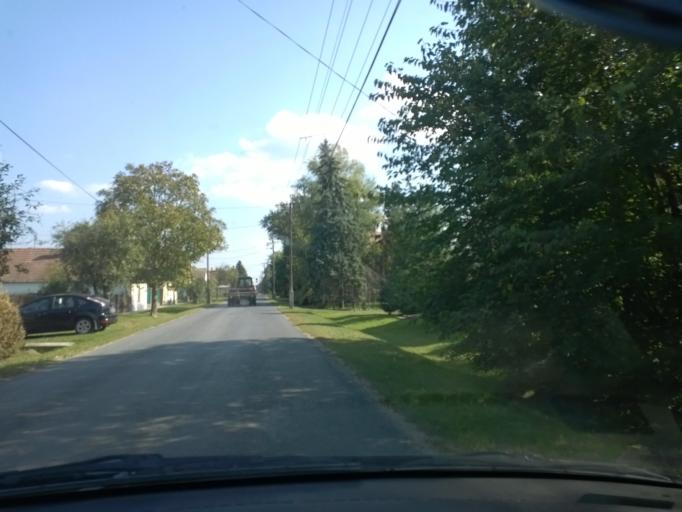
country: HU
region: Bacs-Kiskun
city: Hajos
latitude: 46.4840
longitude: 19.0799
